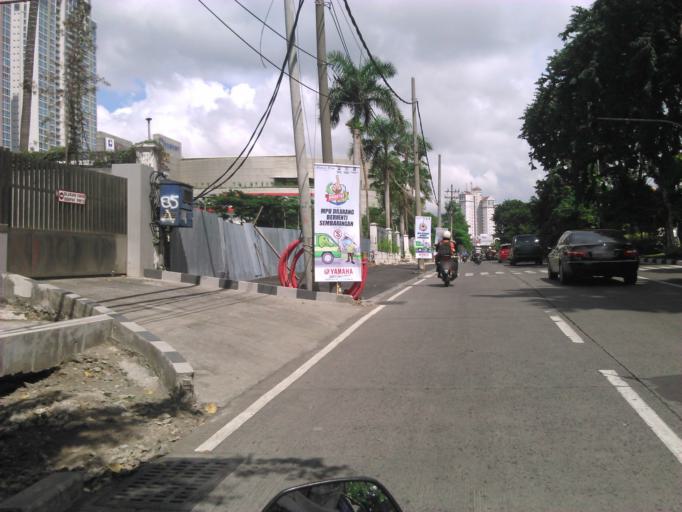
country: ID
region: East Java
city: Jagirsidosermo
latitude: -7.2920
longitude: 112.7217
